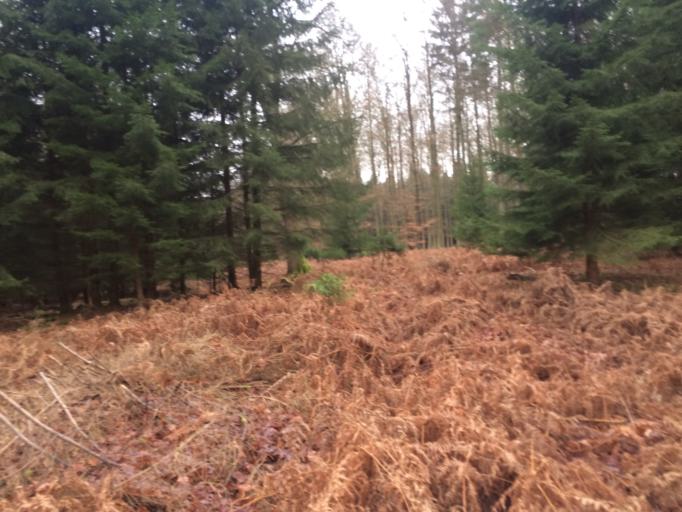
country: DK
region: Capital Region
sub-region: Allerod Kommune
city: Lynge
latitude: 55.8079
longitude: 12.3039
